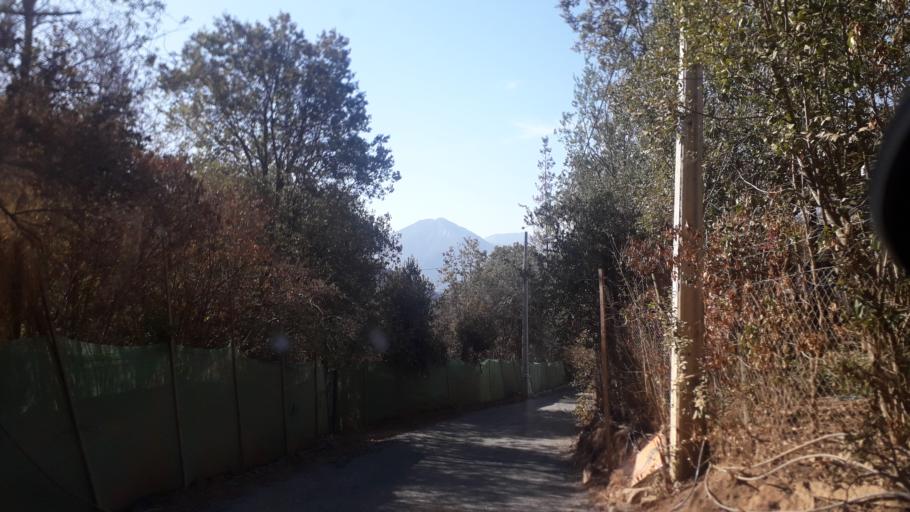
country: CL
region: Valparaiso
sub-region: Provincia de Marga Marga
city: Limache
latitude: -33.0825
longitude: -71.1008
